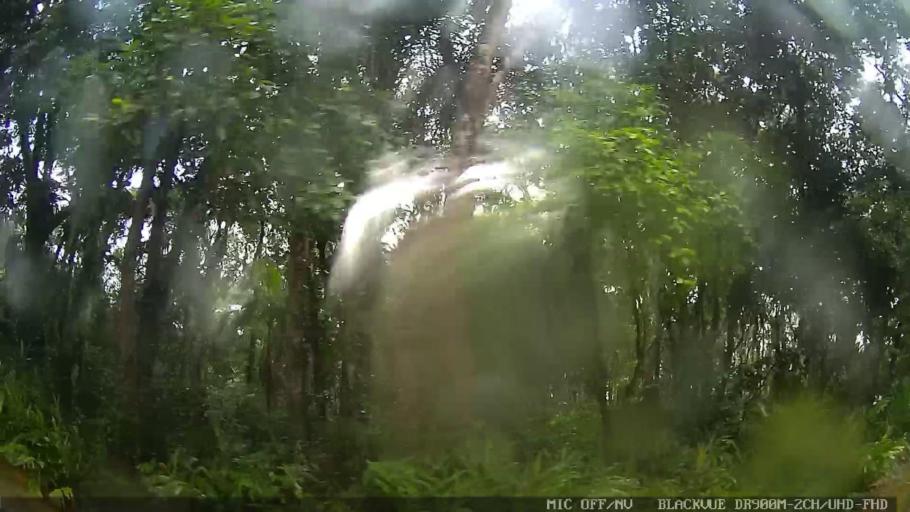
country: BR
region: Sao Paulo
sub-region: Peruibe
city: Peruibe
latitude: -24.2213
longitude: -46.9206
